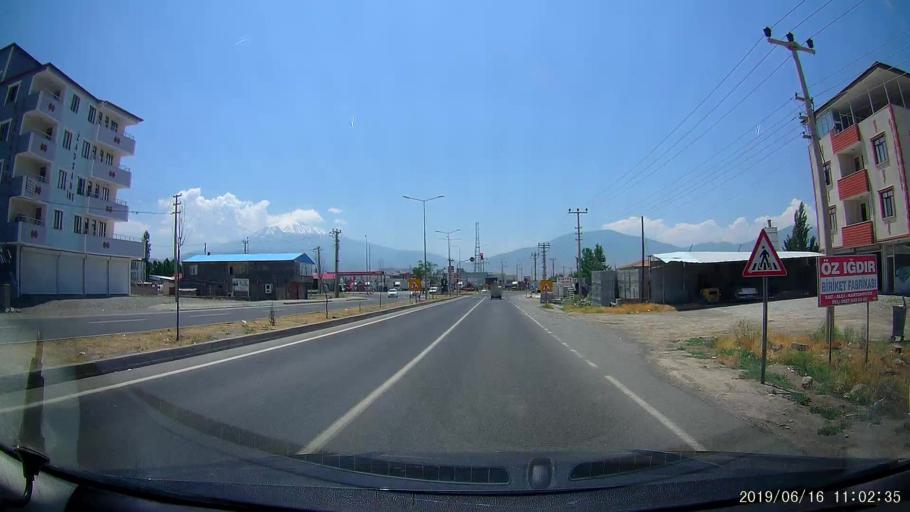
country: TR
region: Igdir
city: Igdir
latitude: 39.9106
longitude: 44.0587
